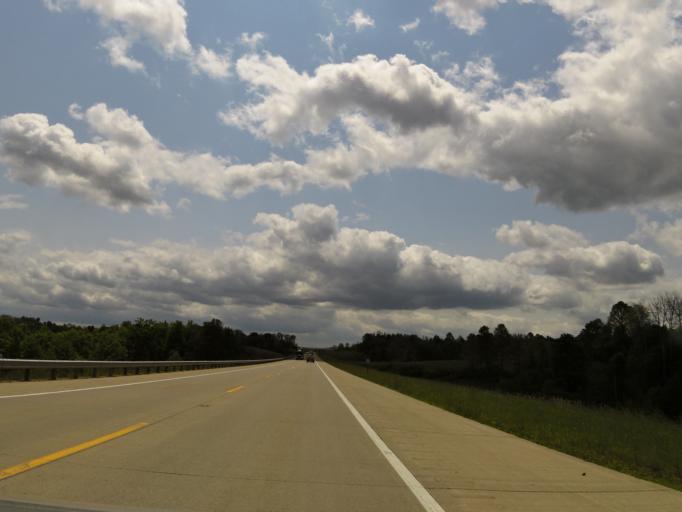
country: US
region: Ohio
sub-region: Athens County
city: Athens
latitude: 39.2659
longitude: -82.0845
